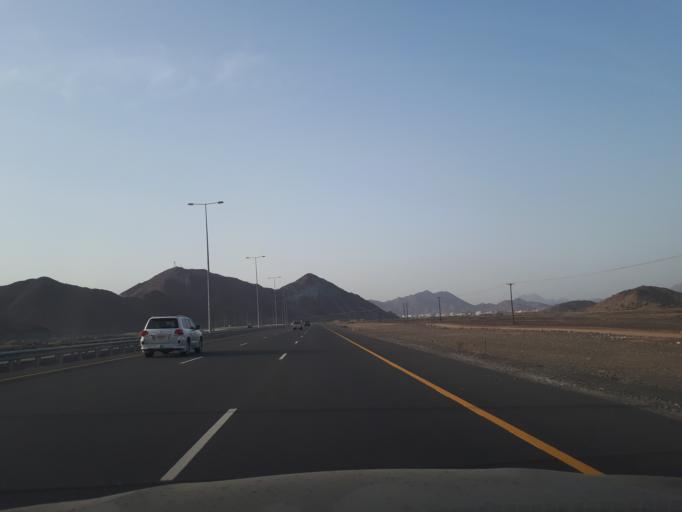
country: OM
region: Muhafazat ad Dakhiliyah
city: Sufalat Sama'il
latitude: 23.3020
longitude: 58.1109
